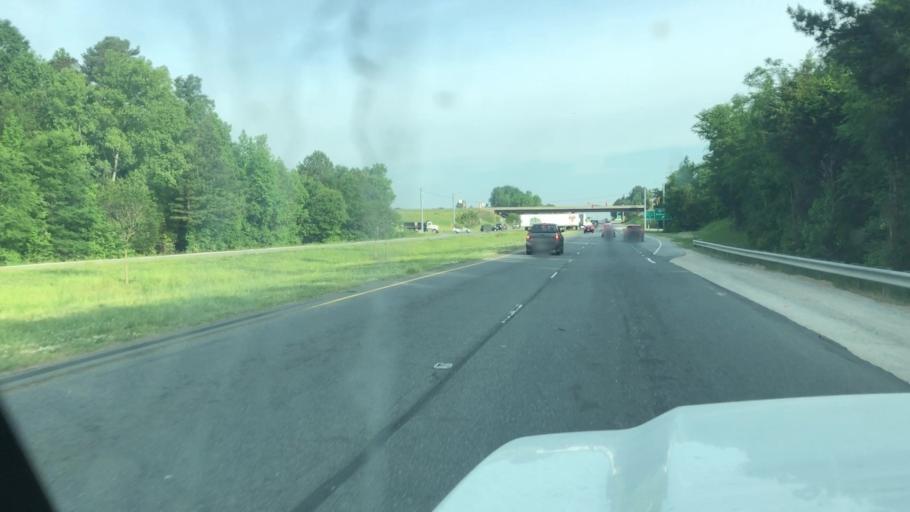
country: US
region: North Carolina
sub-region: Gaston County
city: Mount Holly
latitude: 35.3195
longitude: -80.9374
